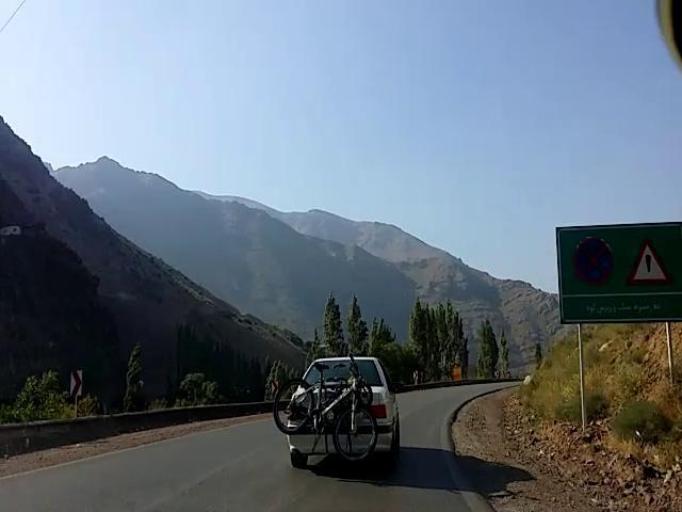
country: IR
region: Tehran
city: Tajrish
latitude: 36.0612
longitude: 51.3093
